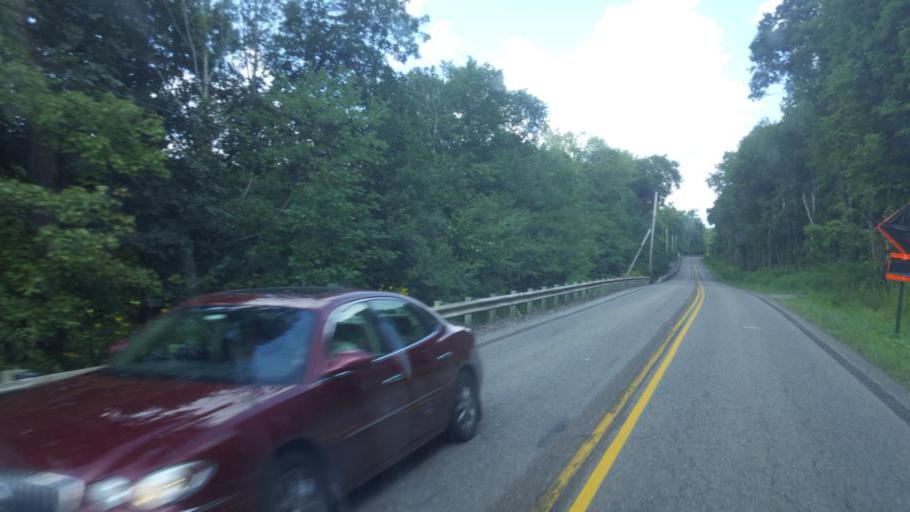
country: US
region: Ohio
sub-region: Columbiana County
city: Lisbon
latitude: 40.7814
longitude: -80.6947
